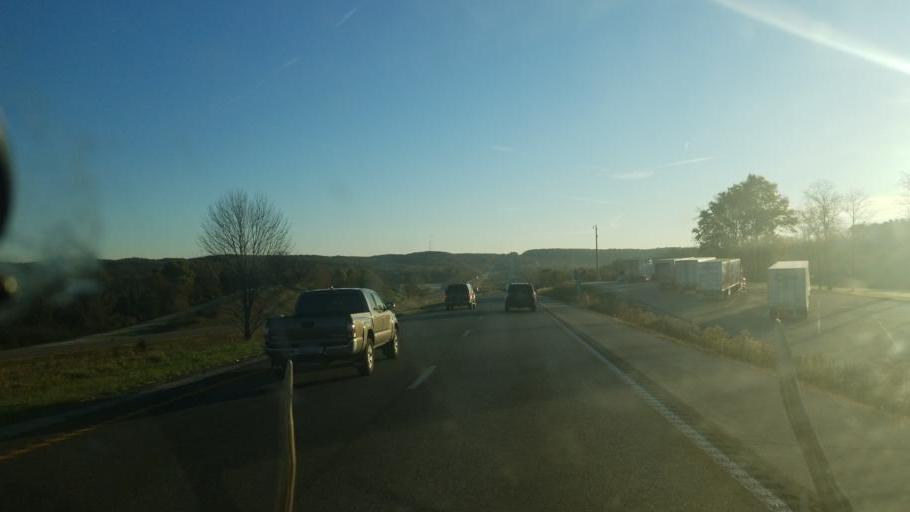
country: US
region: Missouri
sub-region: Montgomery County
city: Montgomery City
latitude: 38.8970
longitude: -91.5998
